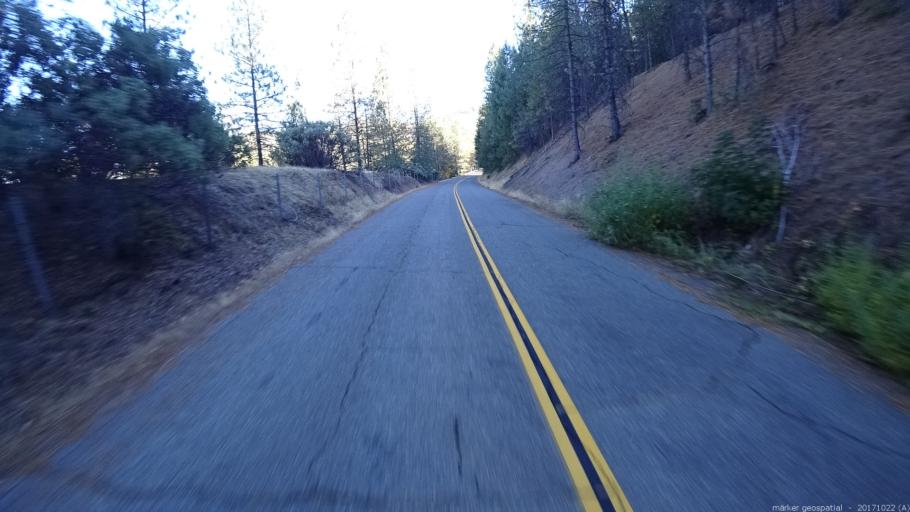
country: US
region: California
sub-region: Shasta County
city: Shasta Lake
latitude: 40.8464
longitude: -122.3361
